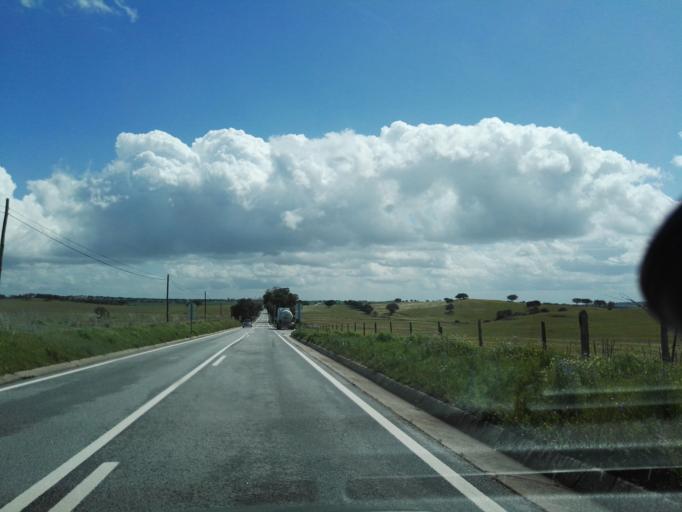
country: PT
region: Portalegre
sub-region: Arronches
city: Arronches
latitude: 39.1227
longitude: -7.2734
